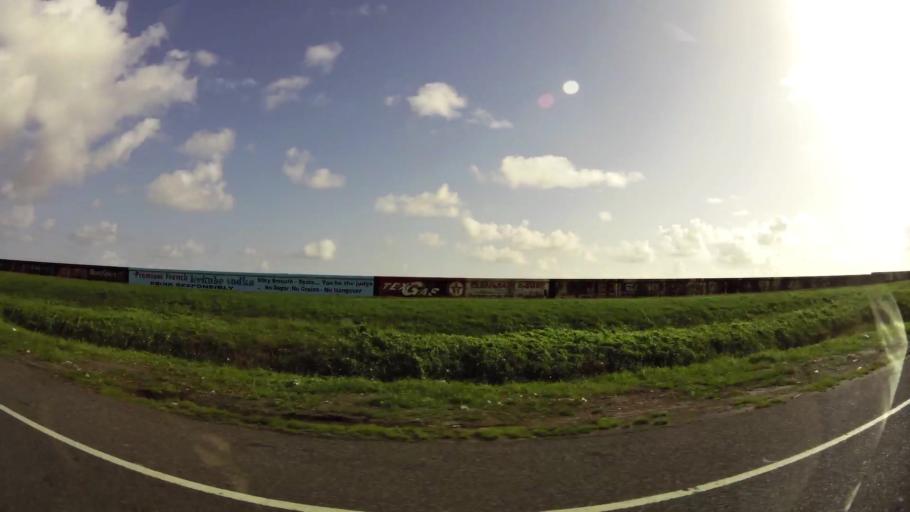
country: GY
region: Demerara-Mahaica
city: Georgetown
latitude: 6.8257
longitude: -58.1173
